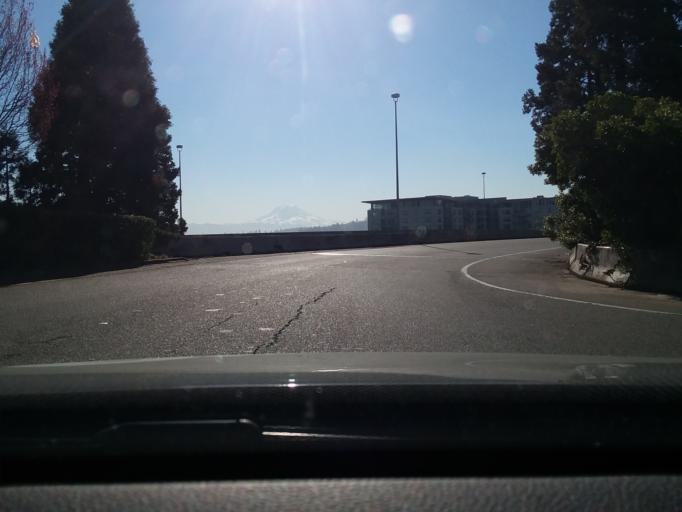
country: US
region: Washington
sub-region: Pierce County
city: Tacoma
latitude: 47.2510
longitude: -122.4363
